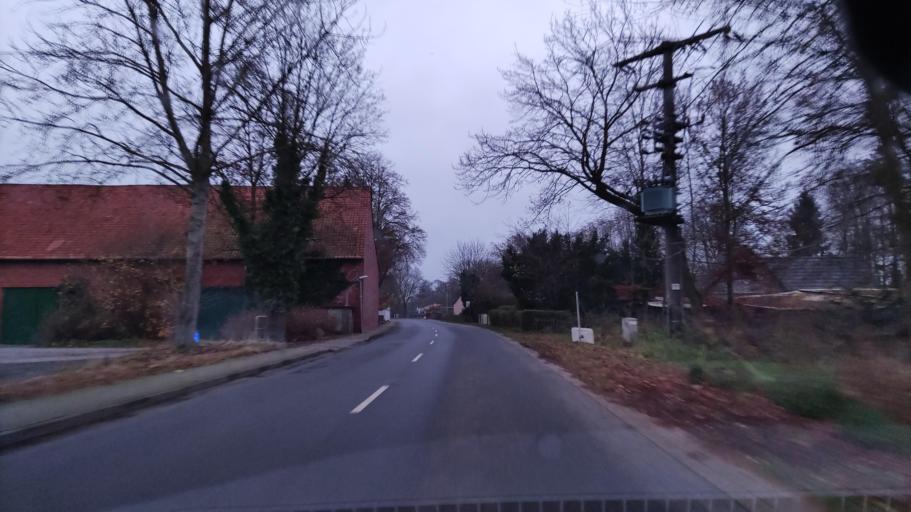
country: DE
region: Lower Saxony
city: Waddeweitz
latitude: 53.0253
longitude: 11.0066
